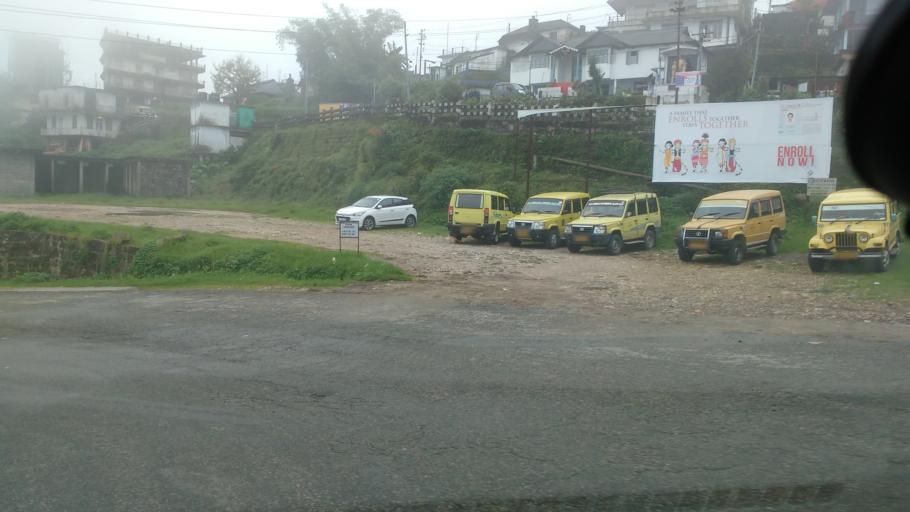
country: IN
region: Meghalaya
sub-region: East Khasi Hills
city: Cherrapunji
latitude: 25.2859
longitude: 91.7202
